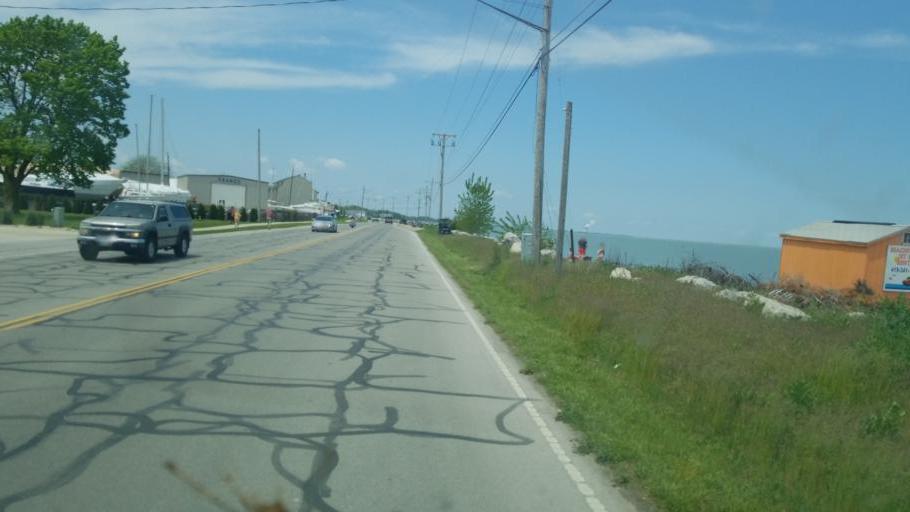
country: US
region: Ohio
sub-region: Ottawa County
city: Port Clinton
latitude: 41.5179
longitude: -82.9460
